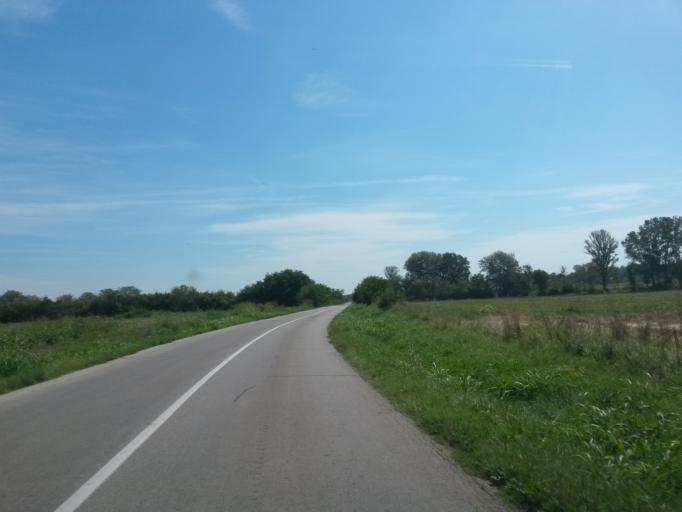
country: HR
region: Vukovarsko-Srijemska
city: Nustar
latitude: 45.3338
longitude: 18.8269
